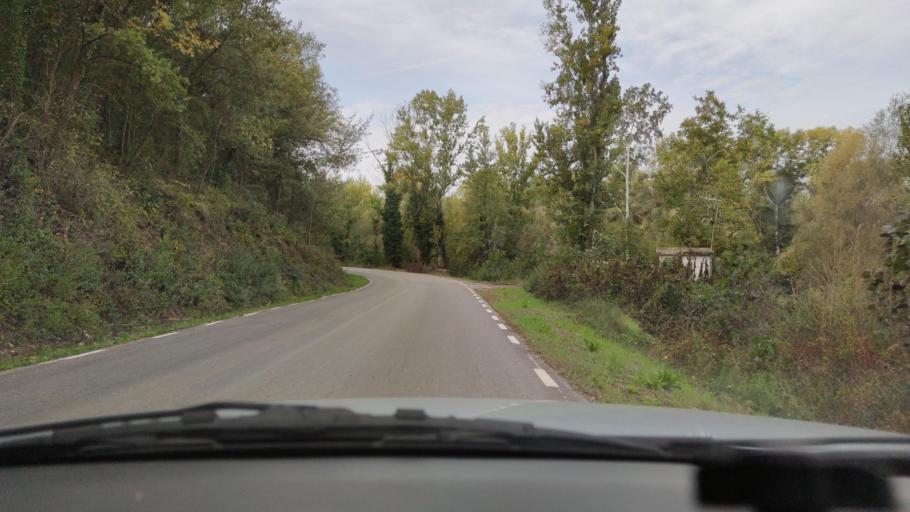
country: ES
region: Catalonia
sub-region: Provincia de Lleida
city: Artesa de Segre
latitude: 41.9172
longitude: 1.0797
